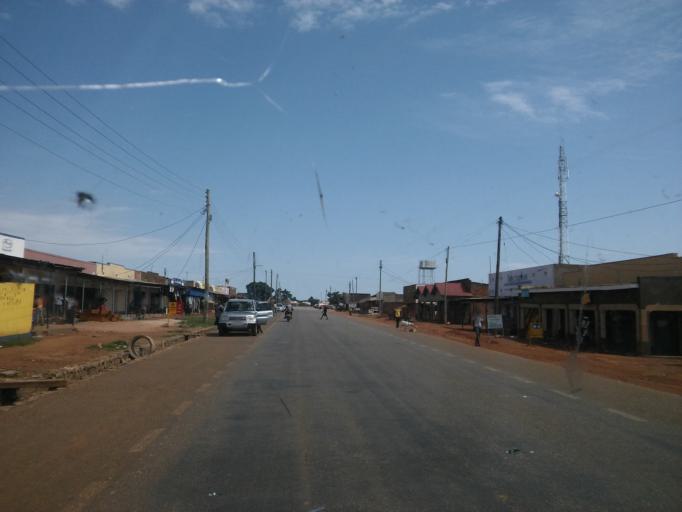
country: UG
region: Eastern Region
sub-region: Bukedea District
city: Bukedea
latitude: 1.3480
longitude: 34.0440
